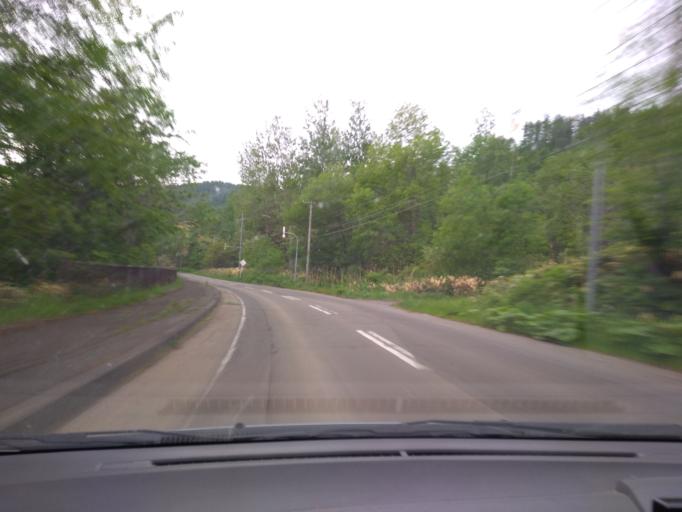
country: JP
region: Hokkaido
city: Shimo-furano
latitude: 43.1723
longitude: 142.5151
